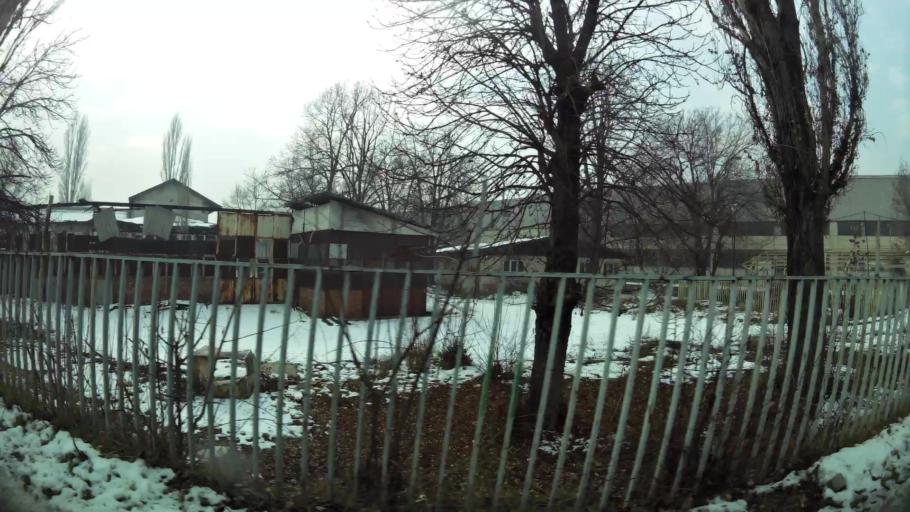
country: MK
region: Cair
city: Cair
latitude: 41.9956
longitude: 21.4580
